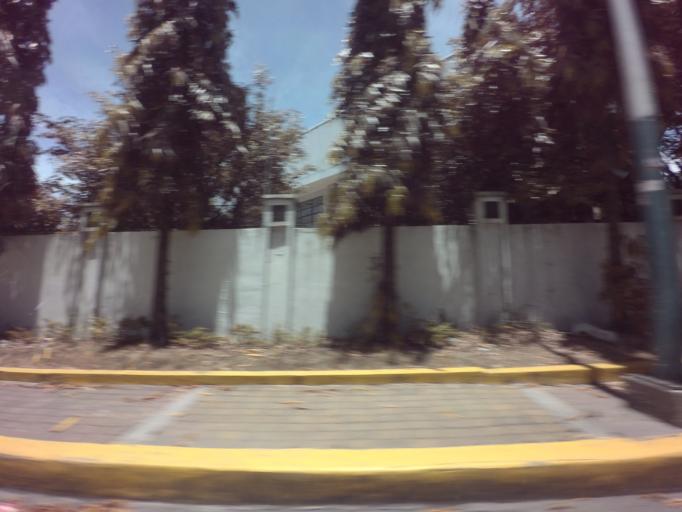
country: PH
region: Metro Manila
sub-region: Makati City
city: Makati City
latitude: 14.5065
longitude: 121.0265
